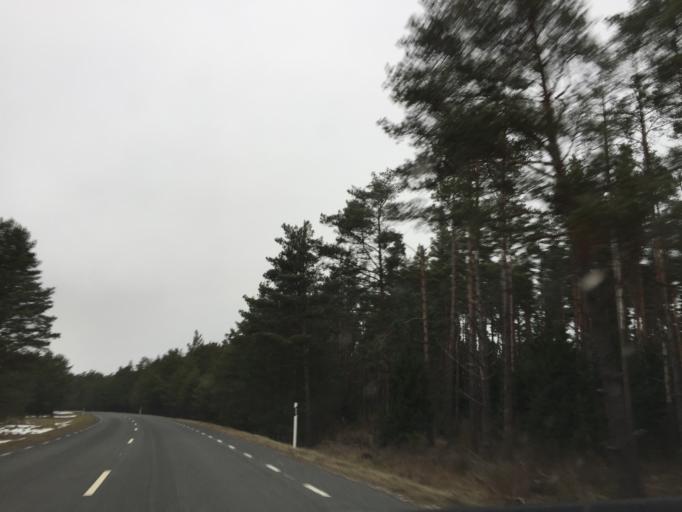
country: EE
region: Saare
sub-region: Kuressaare linn
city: Kuressaare
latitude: 58.5459
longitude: 22.3366
